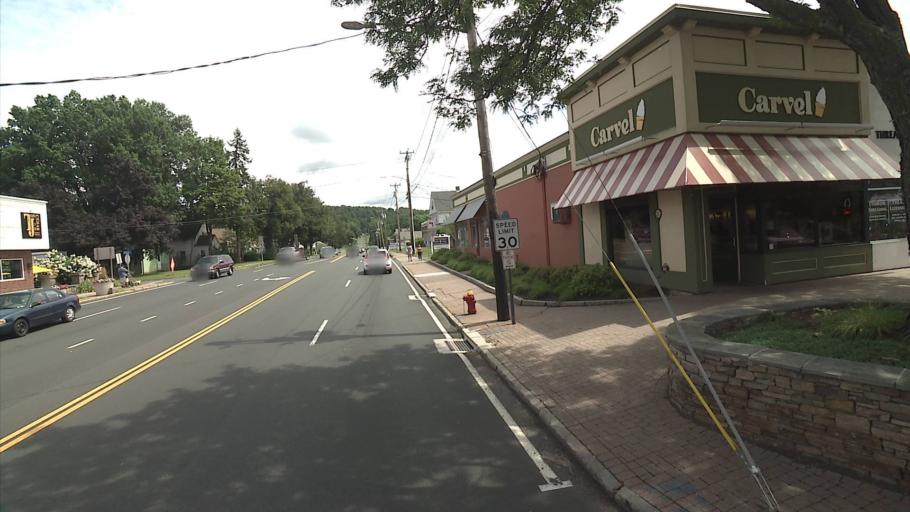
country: US
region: Connecticut
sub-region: Hartford County
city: Newington
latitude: 41.6980
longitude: -72.7233
